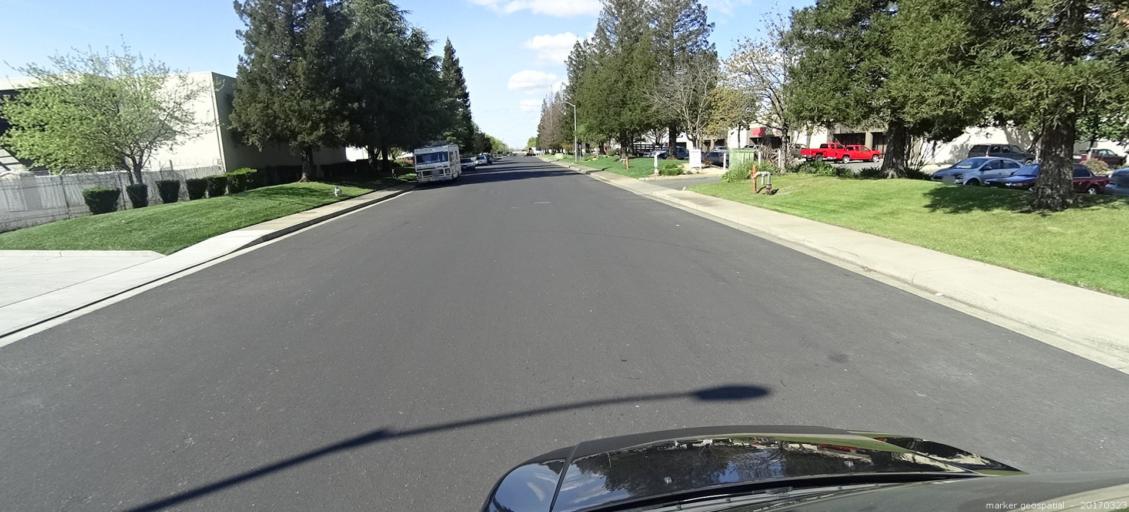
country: US
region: California
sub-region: Sacramento County
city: Florin
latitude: 38.5122
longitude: -121.3848
